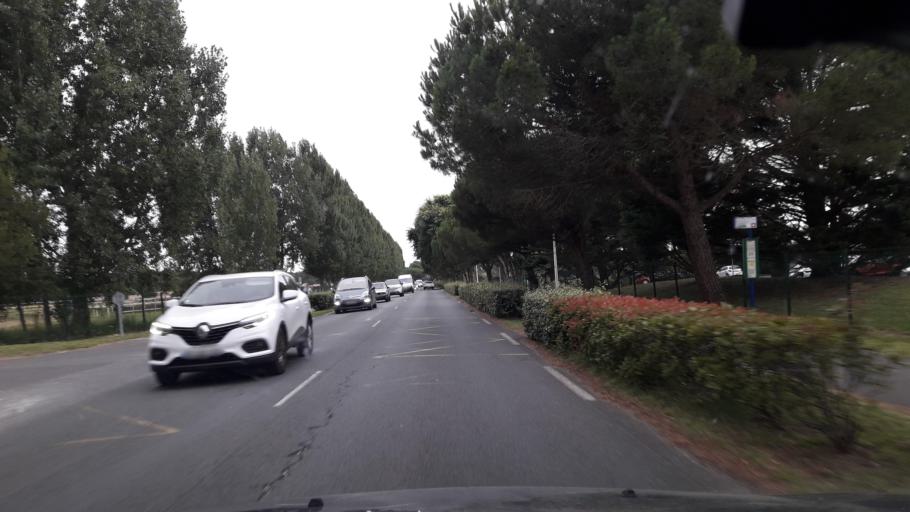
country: FR
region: Poitou-Charentes
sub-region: Departement de la Charente-Maritime
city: Les Mathes
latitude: 45.6994
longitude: -1.1718
